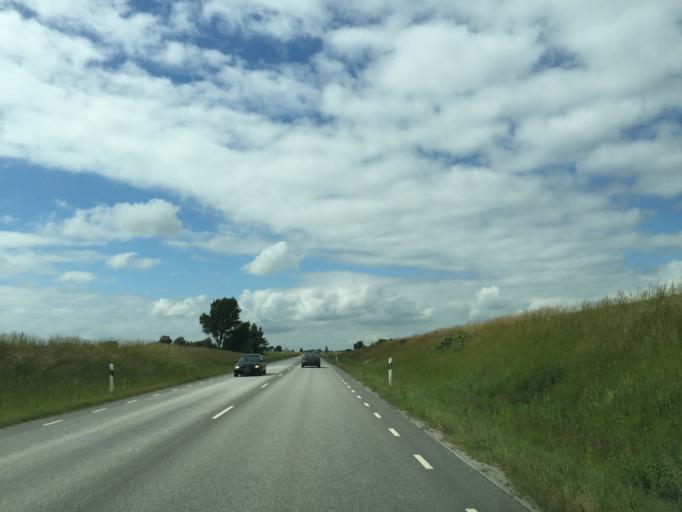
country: SE
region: Skane
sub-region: Staffanstorps Kommun
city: Staffanstorp
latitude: 55.6613
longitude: 13.2113
